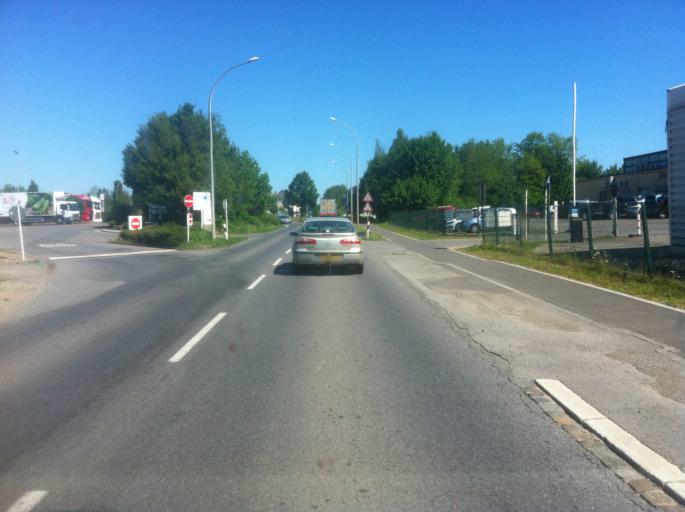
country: LU
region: Luxembourg
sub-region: Canton de Capellen
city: Koerich
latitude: 49.6454
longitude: 5.9558
